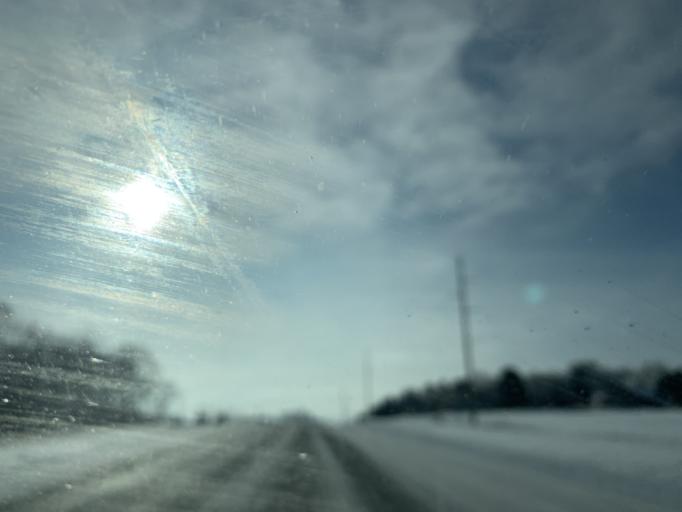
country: US
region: Minnesota
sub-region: Dakota County
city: Lakeville
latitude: 44.6791
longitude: -93.2173
